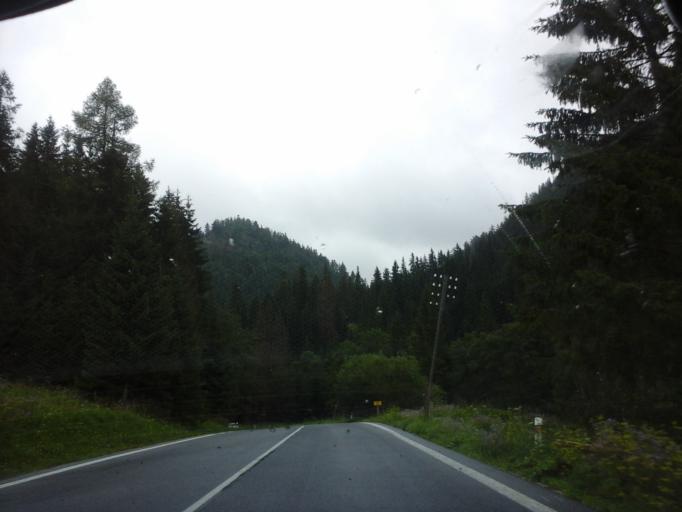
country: SK
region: Kosicky
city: Dobsina
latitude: 48.8748
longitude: 20.2920
